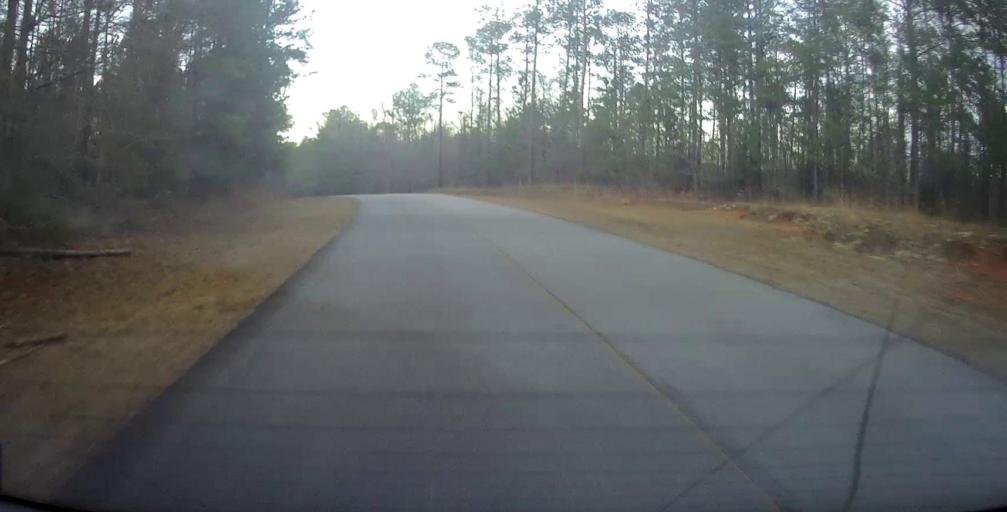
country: US
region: Georgia
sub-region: Harris County
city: Hamilton
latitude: 32.6133
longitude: -84.8530
